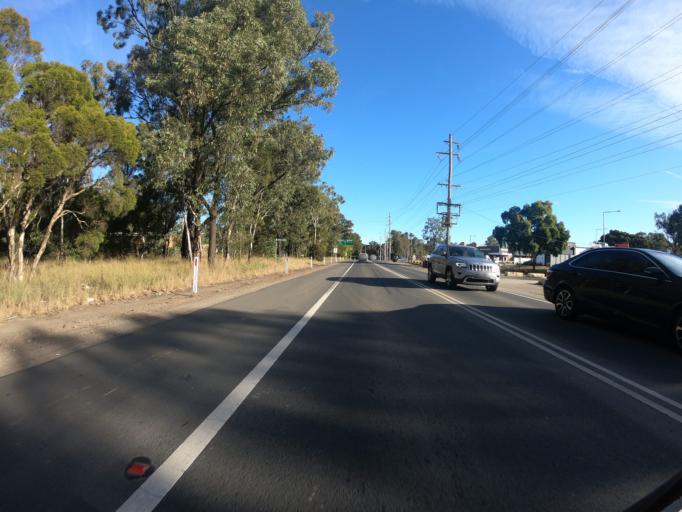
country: AU
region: New South Wales
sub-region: Hawkesbury
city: South Windsor
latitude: -33.6376
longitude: 150.7859
